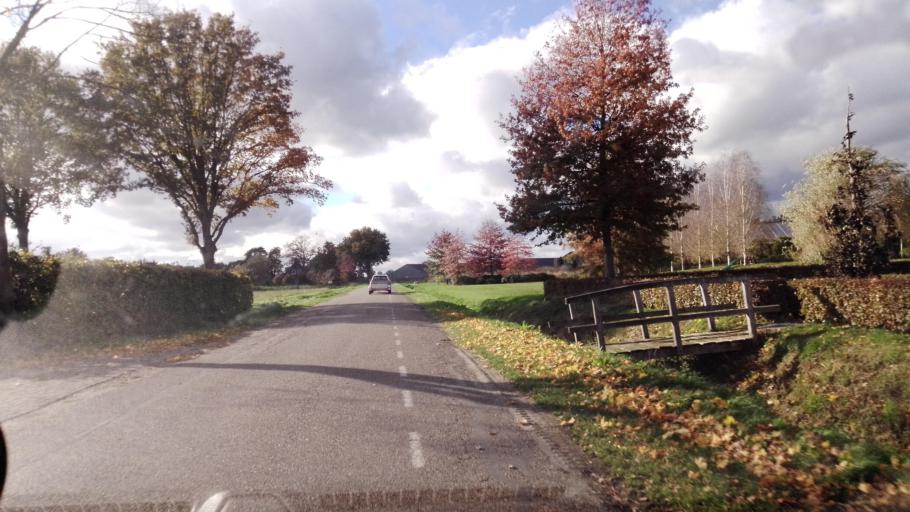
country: NL
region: Limburg
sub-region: Gemeente Venray
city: Venray
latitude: 51.4953
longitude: 5.9551
